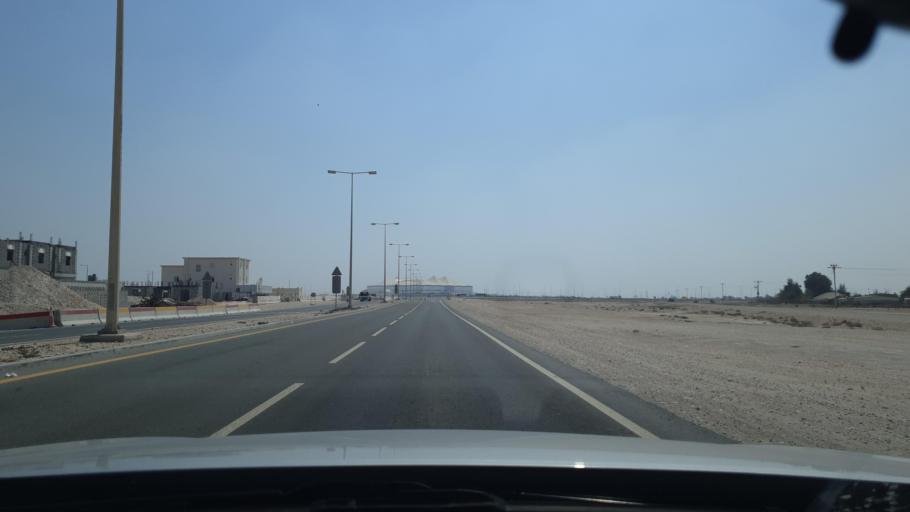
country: QA
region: Al Khawr
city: Al Khawr
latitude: 25.6714
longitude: 51.4711
